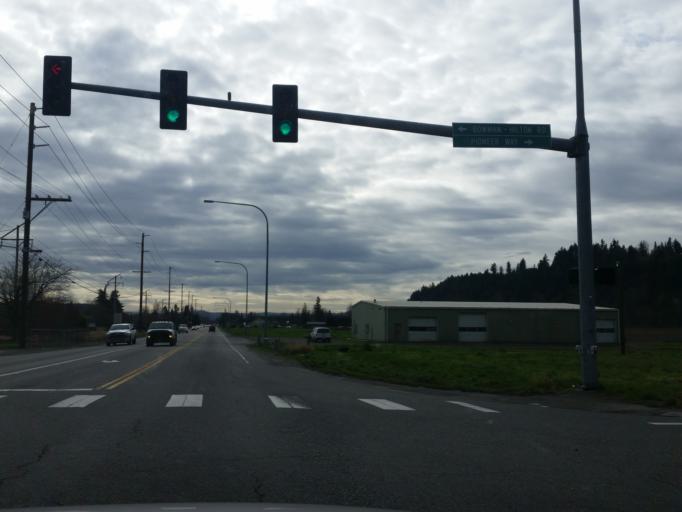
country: US
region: Washington
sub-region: Pierce County
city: Alderton
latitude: 47.1807
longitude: -122.2294
